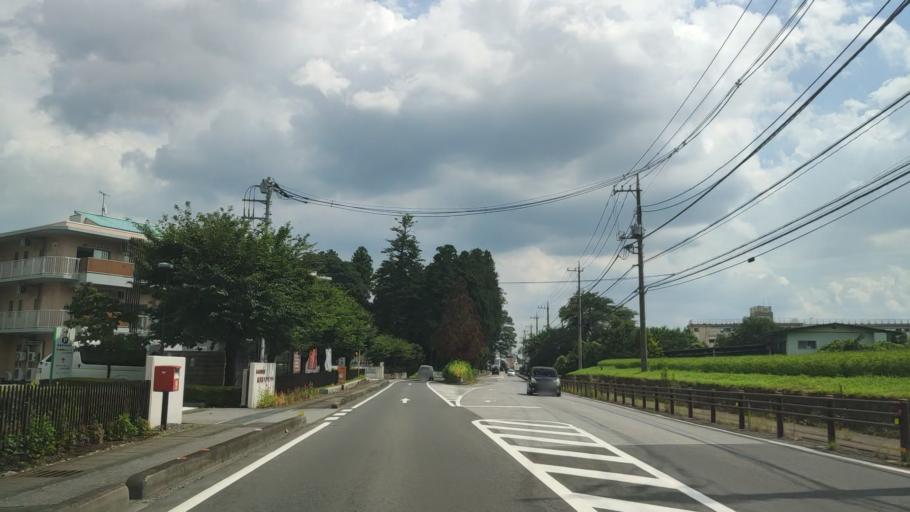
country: JP
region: Tochigi
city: Utsunomiya-shi
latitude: 36.6583
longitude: 139.8398
